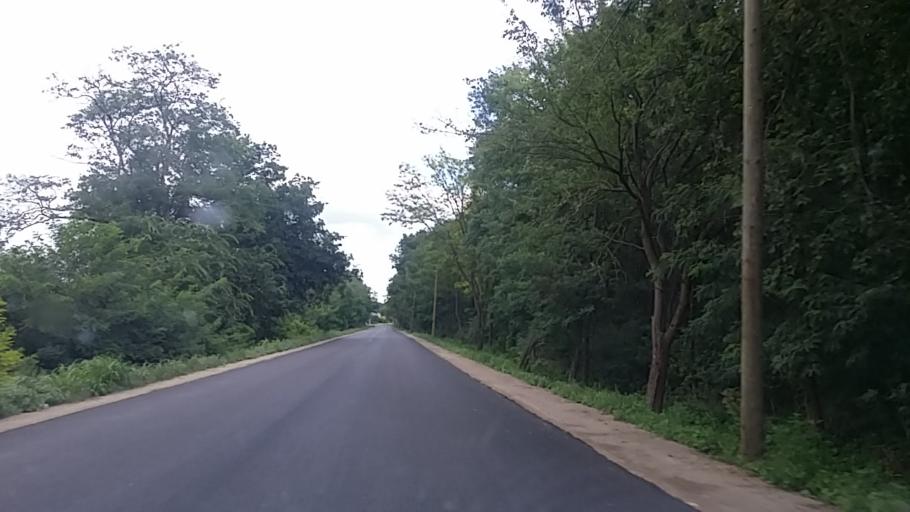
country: HU
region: Tolna
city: Tengelic
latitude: 46.5466
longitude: 18.6923
